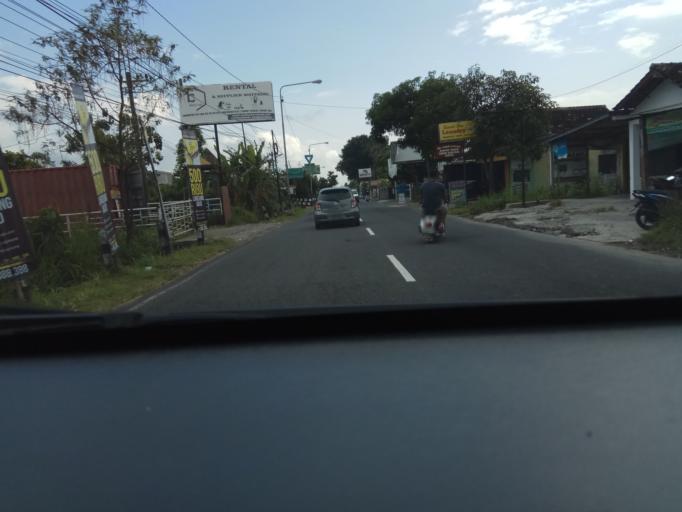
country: ID
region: Daerah Istimewa Yogyakarta
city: Melati
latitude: -7.7135
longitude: 110.4074
